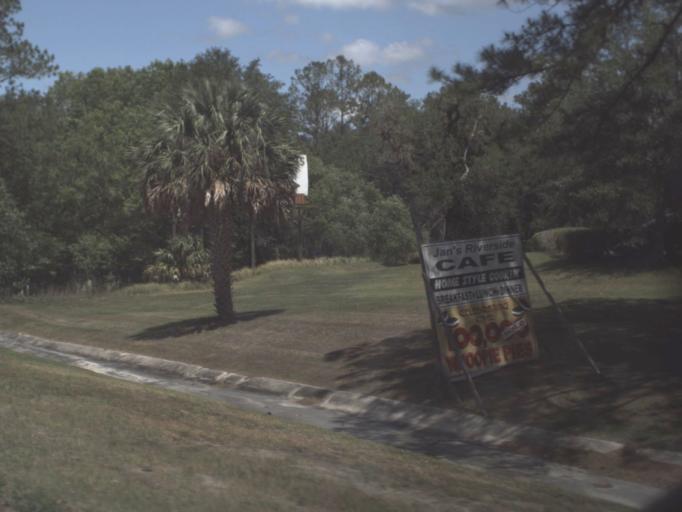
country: US
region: Florida
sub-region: Marion County
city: Silver Springs Shores
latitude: 29.2141
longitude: -81.9821
